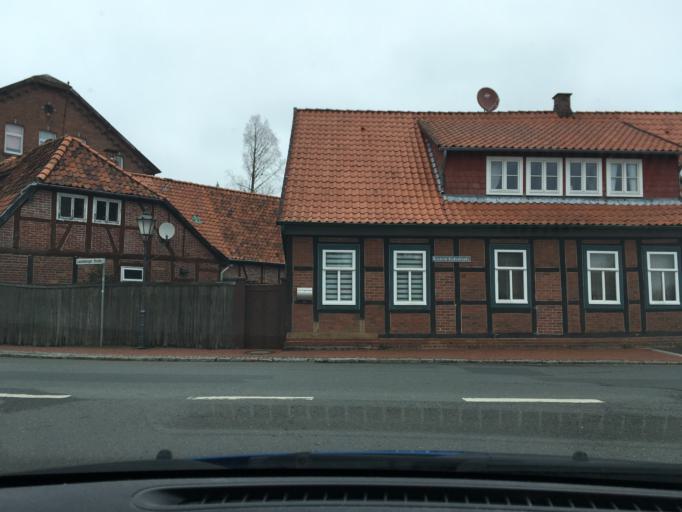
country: DE
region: Lower Saxony
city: Bleckede
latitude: 53.2934
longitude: 10.7274
